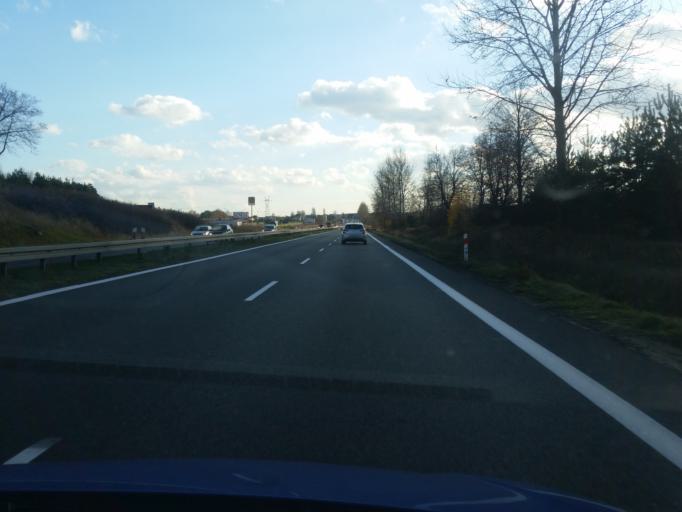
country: PL
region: Silesian Voivodeship
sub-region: Powiat bedzinski
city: Siewierz
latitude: 50.5160
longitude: 19.1942
